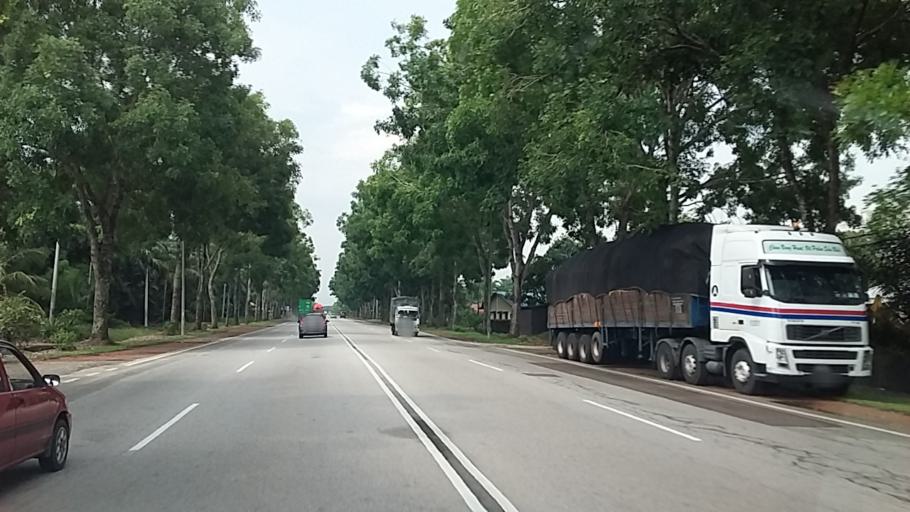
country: MY
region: Johor
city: Parit Raja
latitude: 1.8715
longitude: 103.1307
